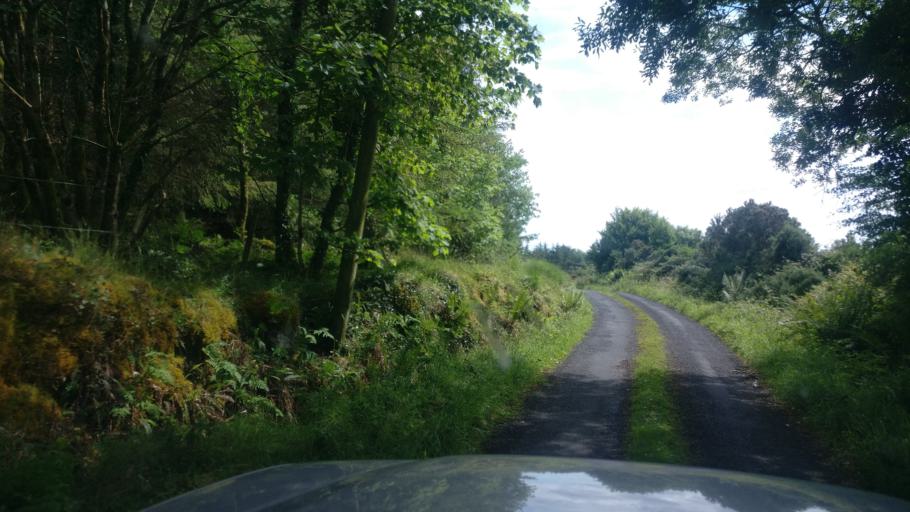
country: IE
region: Connaught
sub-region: County Galway
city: Gort
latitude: 53.0752
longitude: -8.7086
